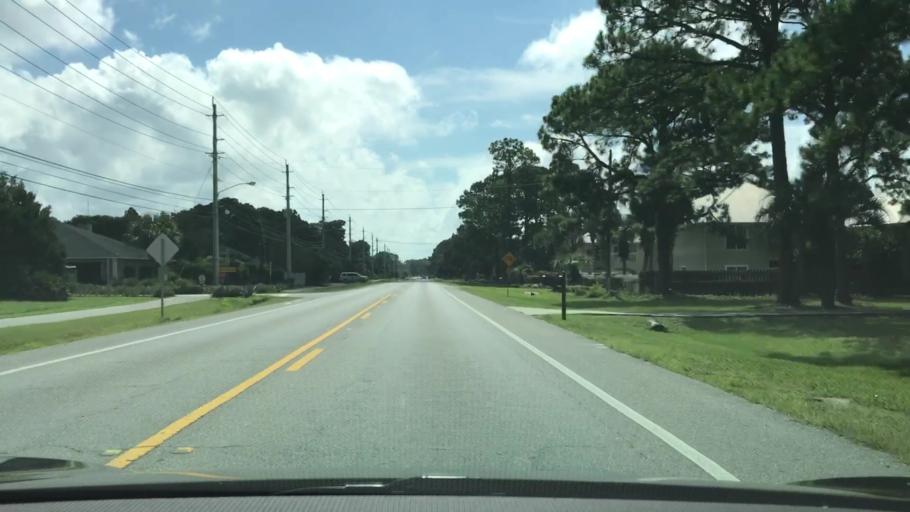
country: US
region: Florida
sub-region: Bay County
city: Lower Grand Lagoon
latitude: 30.1610
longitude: -85.7648
